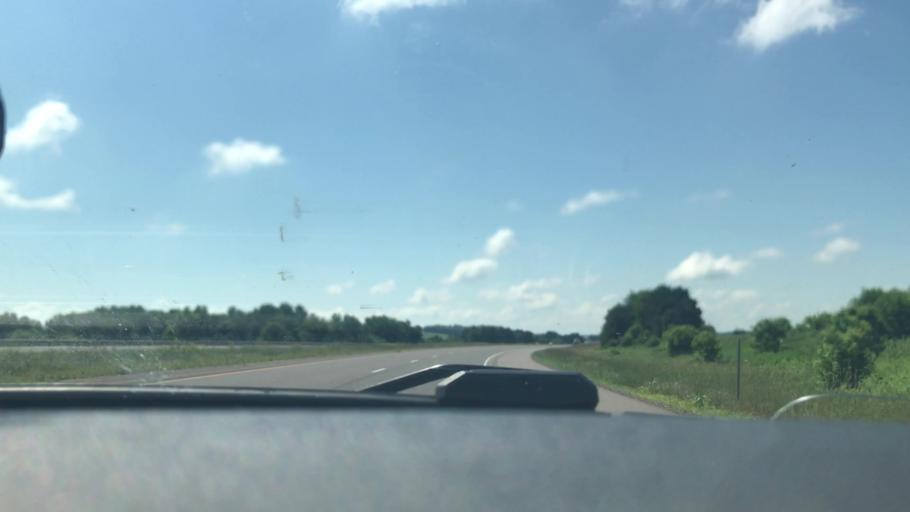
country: US
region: Wisconsin
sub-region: Chippewa County
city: Bloomer
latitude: 45.0650
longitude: -91.4667
